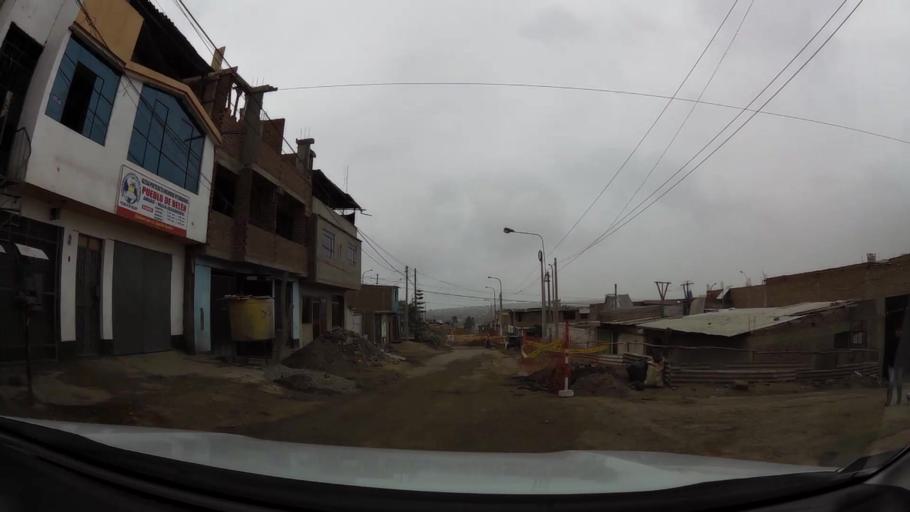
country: PE
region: Lima
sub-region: Lima
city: Punta Hermosa
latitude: -12.2368
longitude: -76.9070
